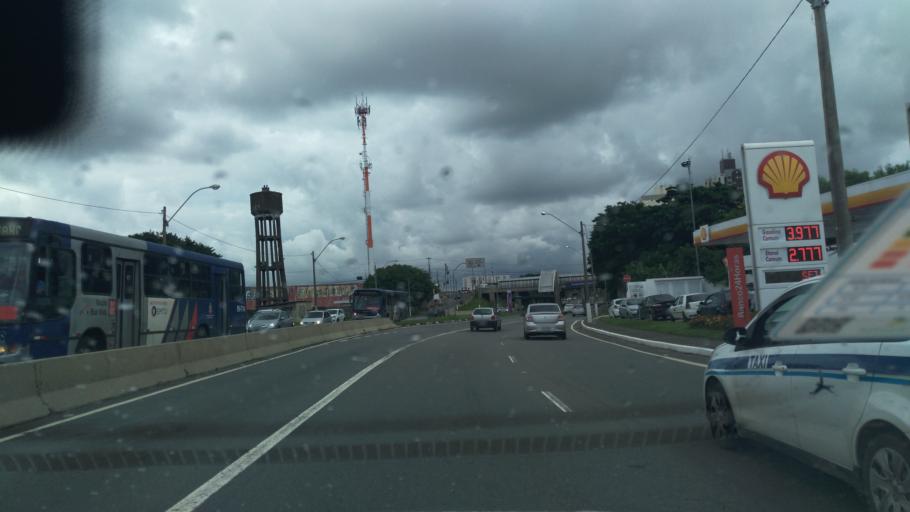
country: BR
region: Sao Paulo
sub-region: Campinas
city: Campinas
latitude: -22.9023
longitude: -47.0802
